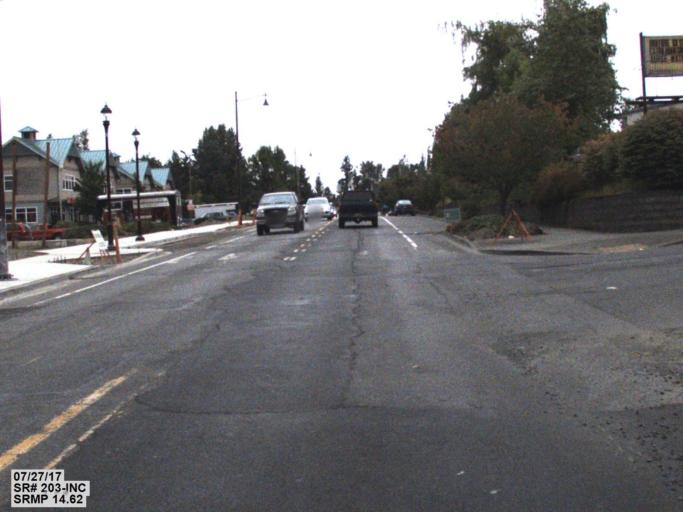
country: US
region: Washington
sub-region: King County
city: Duvall
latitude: 47.7379
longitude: -121.9871
